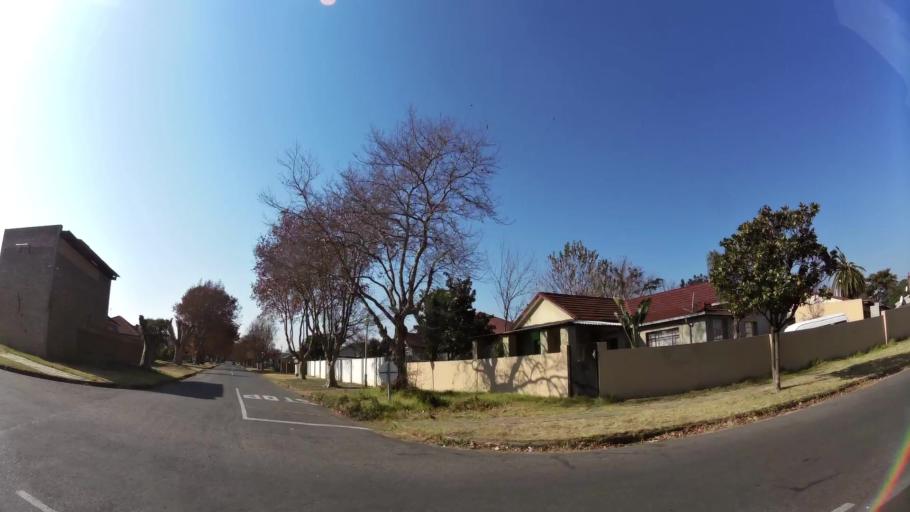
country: ZA
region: Gauteng
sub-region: Ekurhuleni Metropolitan Municipality
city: Boksburg
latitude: -26.2212
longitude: 28.2583
